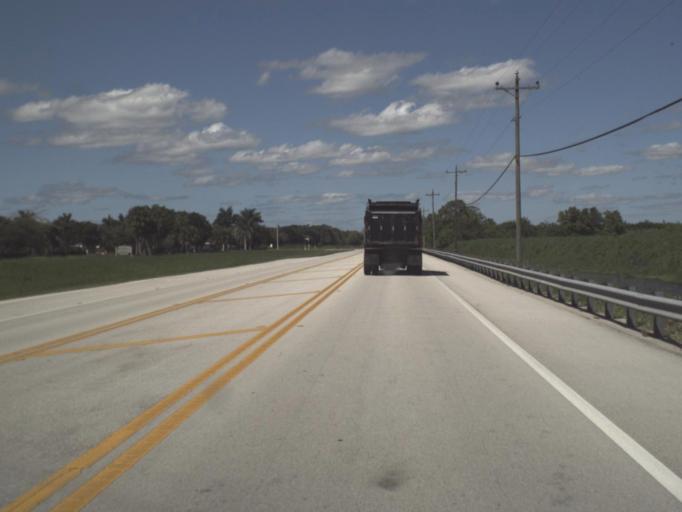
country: US
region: Florida
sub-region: Collier County
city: Lely Resort
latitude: 26.0154
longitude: -81.6243
